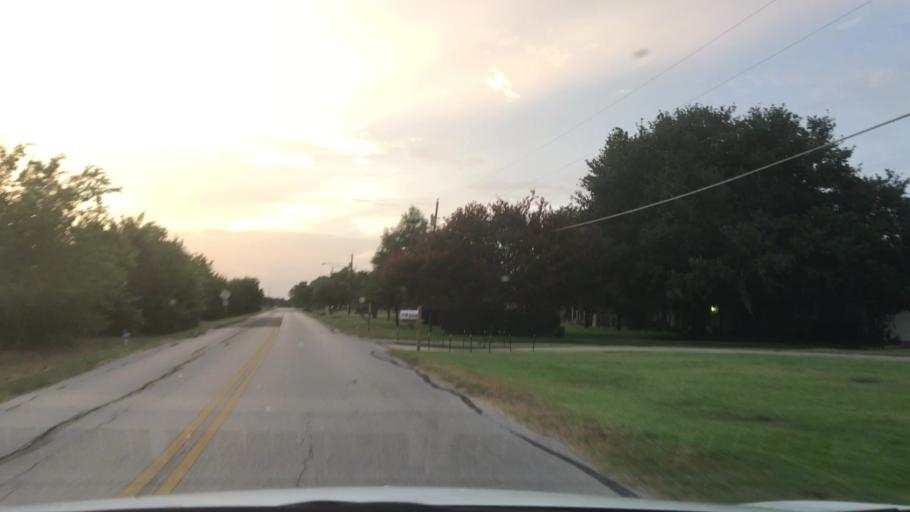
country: US
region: Texas
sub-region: Dallas County
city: Seagoville
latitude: 32.6973
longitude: -96.5496
